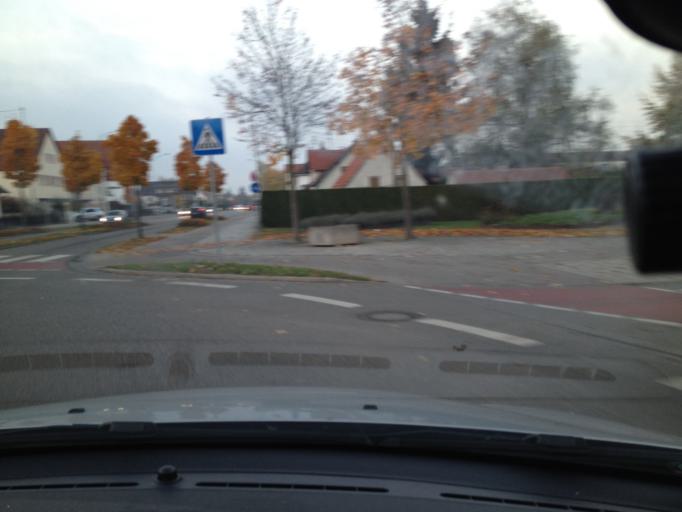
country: DE
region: Bavaria
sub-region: Swabia
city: Konigsbrunn
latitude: 48.2728
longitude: 10.8895
